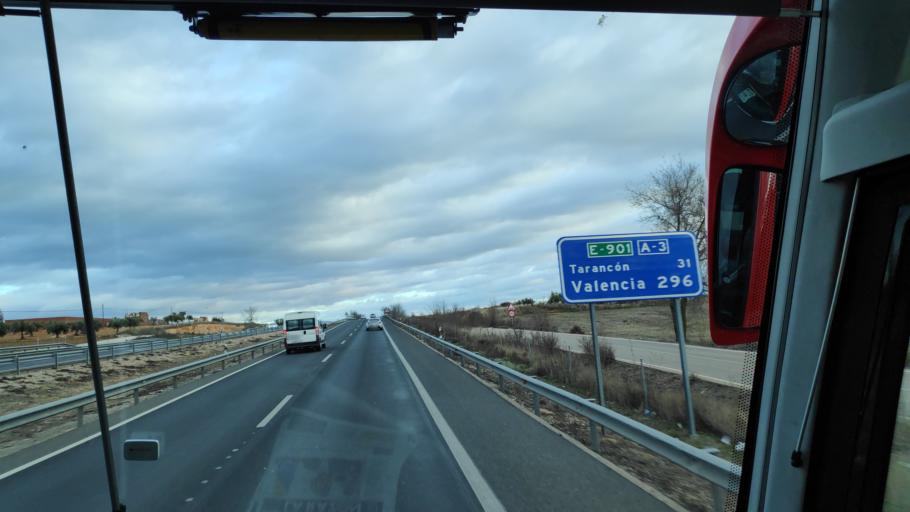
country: ES
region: Madrid
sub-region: Provincia de Madrid
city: Villarejo de Salvanes
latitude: 40.1598
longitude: -3.2624
